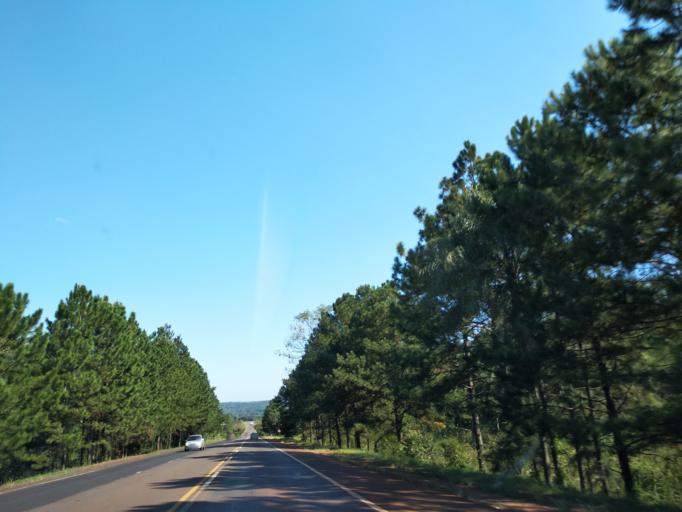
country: AR
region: Misiones
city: Caraguatay
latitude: -26.6334
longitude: -54.7501
